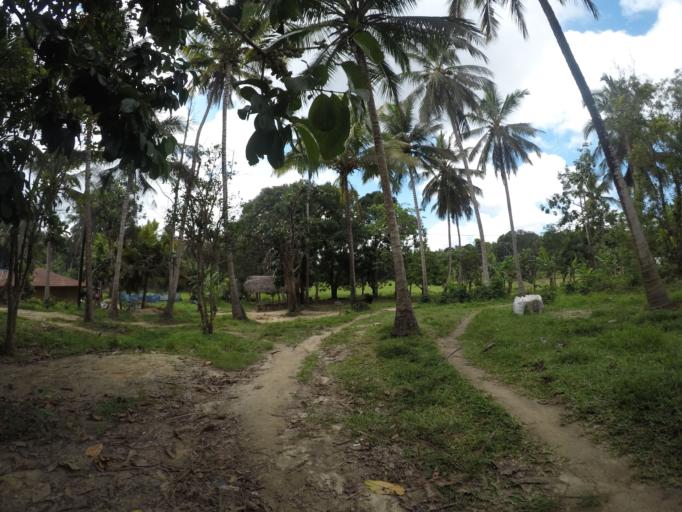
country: TZ
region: Pemba South
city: Mtambile
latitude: -5.3816
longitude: 39.7174
